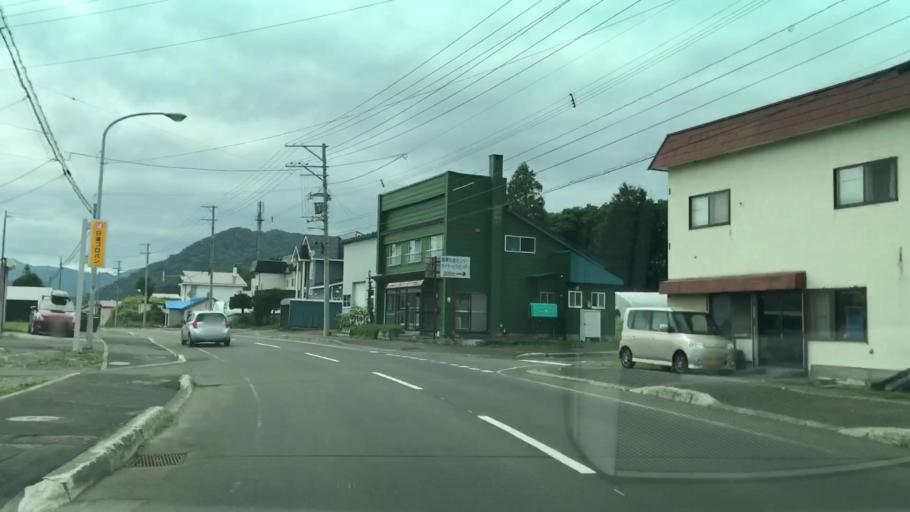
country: JP
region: Hokkaido
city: Yoichi
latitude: 43.0885
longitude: 140.8154
